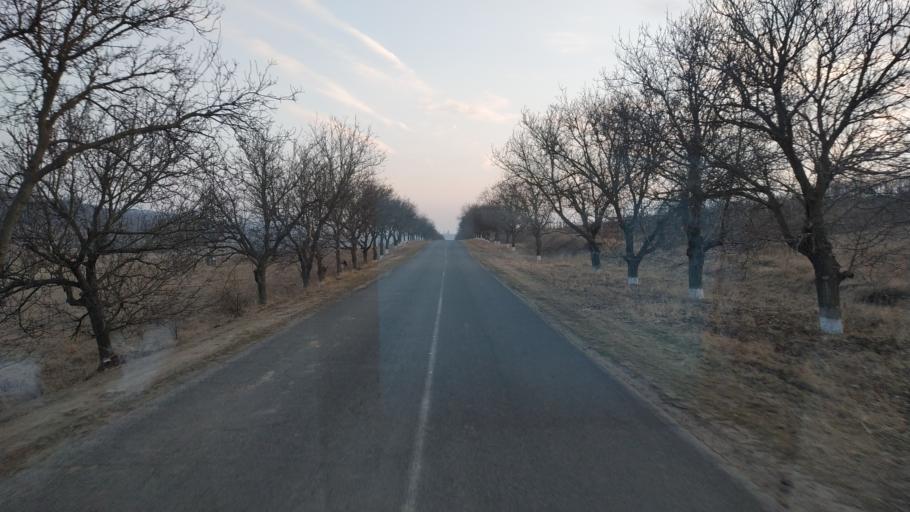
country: MD
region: Hincesti
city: Dancu
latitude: 46.6870
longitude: 28.3358
